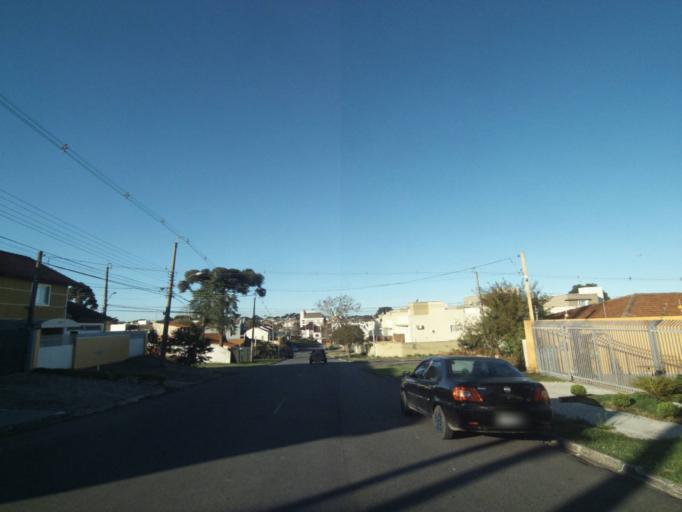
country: BR
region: Parana
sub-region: Curitiba
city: Curitiba
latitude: -25.3888
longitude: -49.2482
